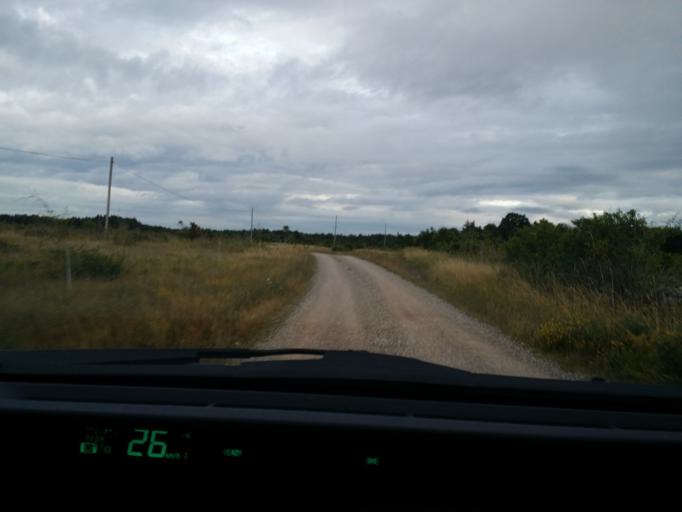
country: SE
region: Kalmar
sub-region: Borgholms Kommun
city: Borgholm
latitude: 57.2128
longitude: 16.9499
